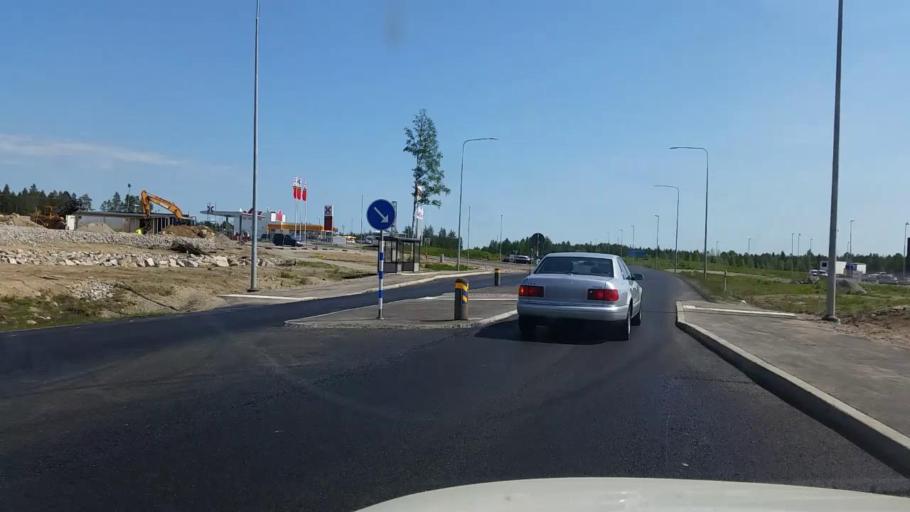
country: SE
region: Gaevleborg
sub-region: Hudiksvalls Kommun
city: Sorforsa
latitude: 61.7144
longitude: 17.0421
